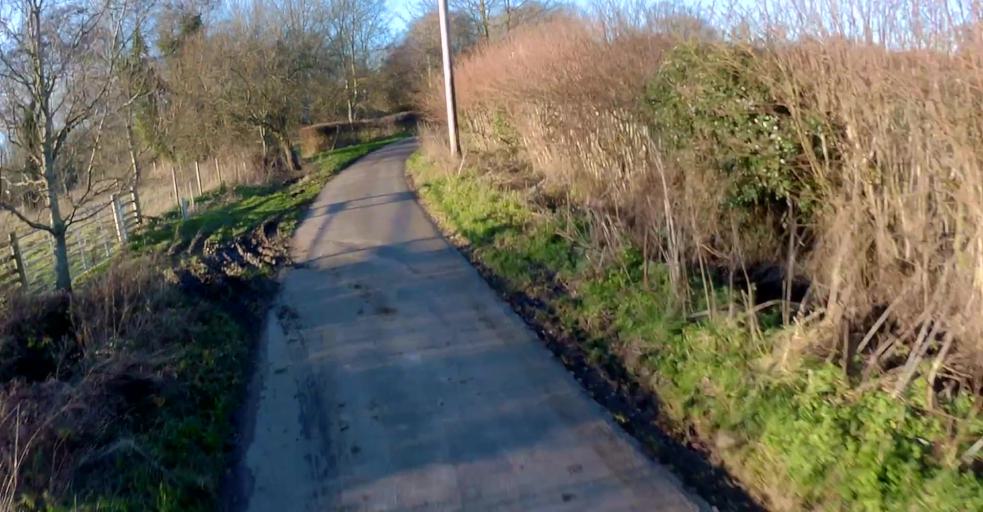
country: GB
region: England
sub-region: Hampshire
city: Hook
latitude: 51.3082
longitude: -1.0007
